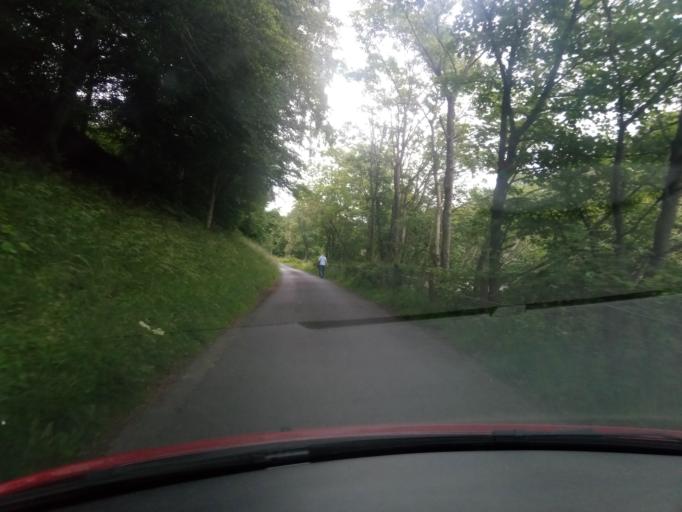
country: GB
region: Scotland
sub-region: The Scottish Borders
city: Hawick
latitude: 55.4146
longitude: -2.8194
